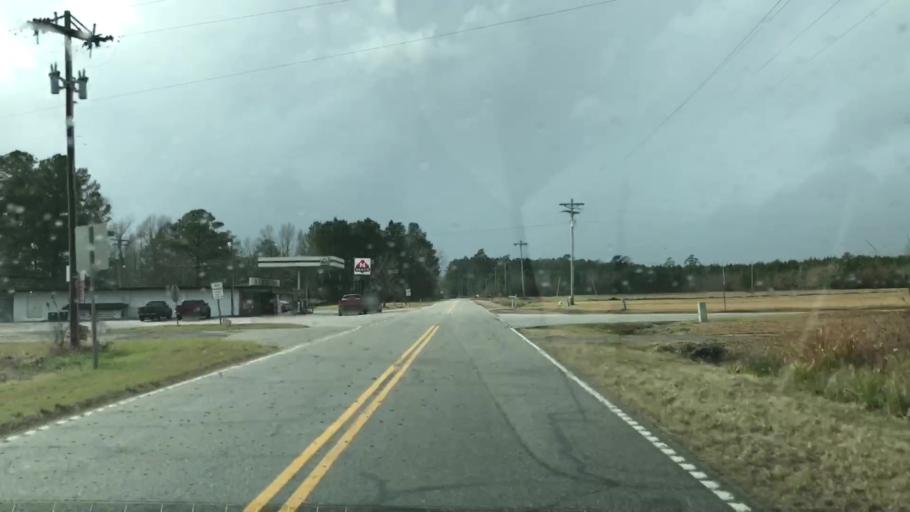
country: US
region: South Carolina
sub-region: Florence County
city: Johnsonville
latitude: 33.6784
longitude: -79.3832
